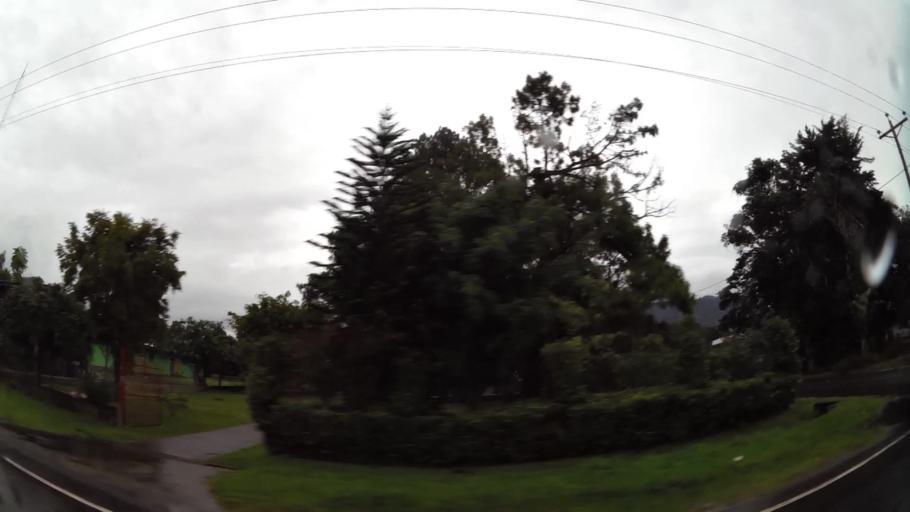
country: PA
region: Chiriqui
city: Volcan
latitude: 8.7762
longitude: -82.6371
